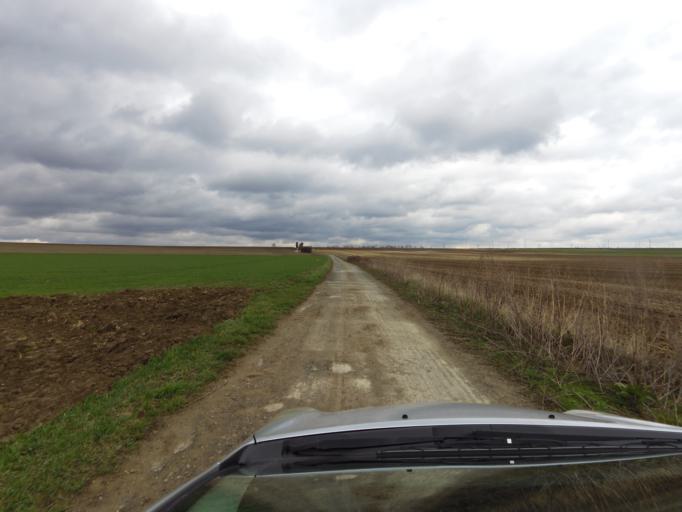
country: FR
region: Nord-Pas-de-Calais
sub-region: Departement du Pas-de-Calais
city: Beaurains
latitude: 50.2216
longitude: 2.7900
